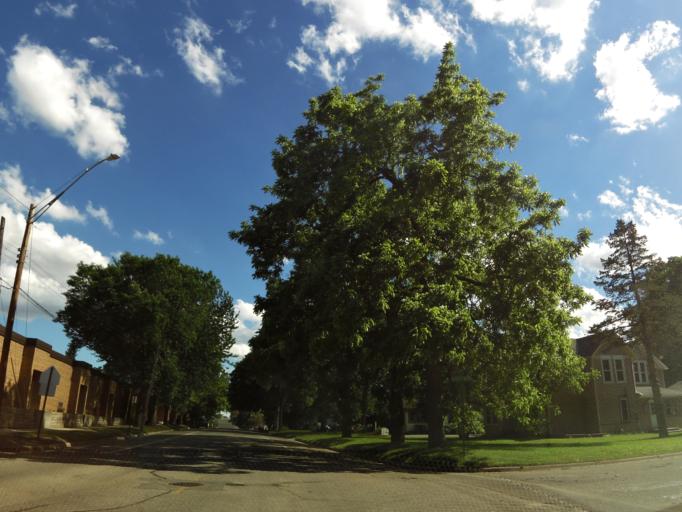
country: US
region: Minnesota
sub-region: Meeker County
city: Dassel
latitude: 45.0836
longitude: -94.3074
